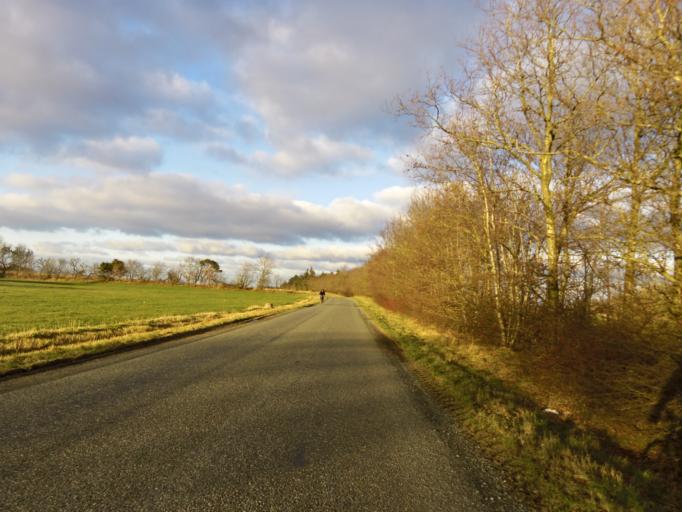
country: DK
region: South Denmark
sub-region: Esbjerg Kommune
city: Ribe
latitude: 55.2948
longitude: 8.8482
